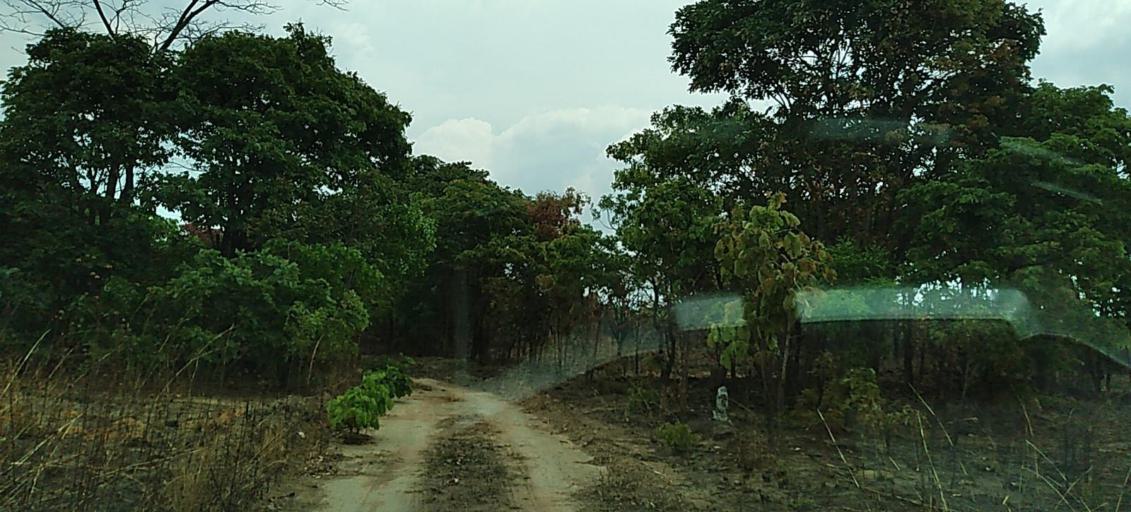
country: ZM
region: Copperbelt
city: Chililabombwe
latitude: -12.3267
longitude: 27.7715
